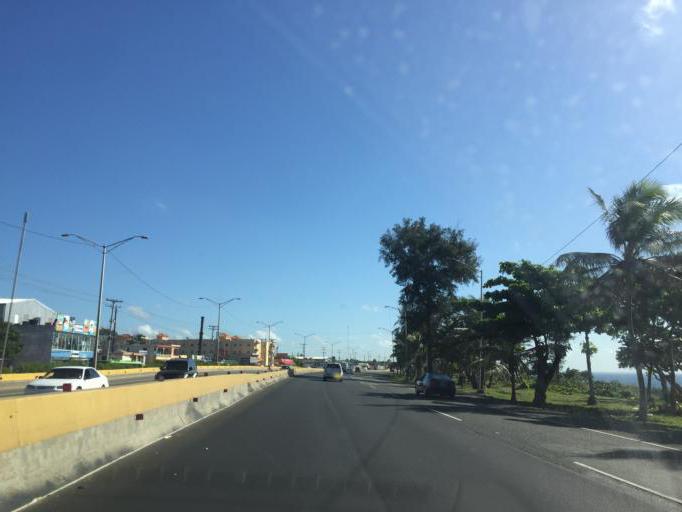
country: DO
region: Santo Domingo
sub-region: Santo Domingo
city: Santo Domingo Este
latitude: 18.4659
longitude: -69.7960
